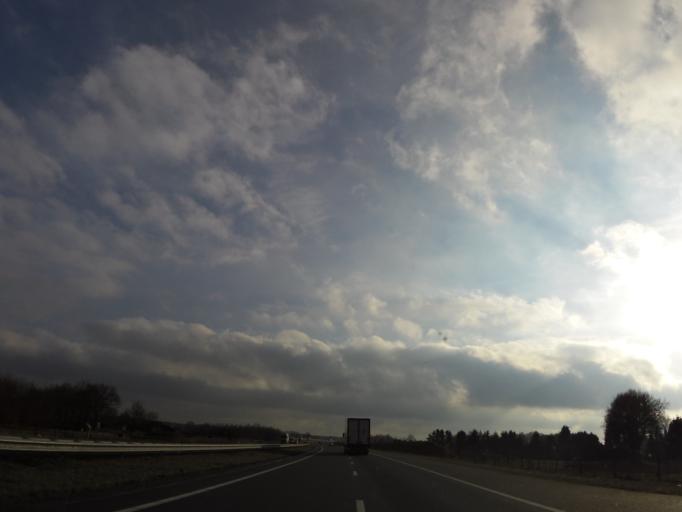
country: NL
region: Limburg
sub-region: Gemeente Beesel
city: Offenbeek
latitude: 51.2870
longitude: 6.1005
